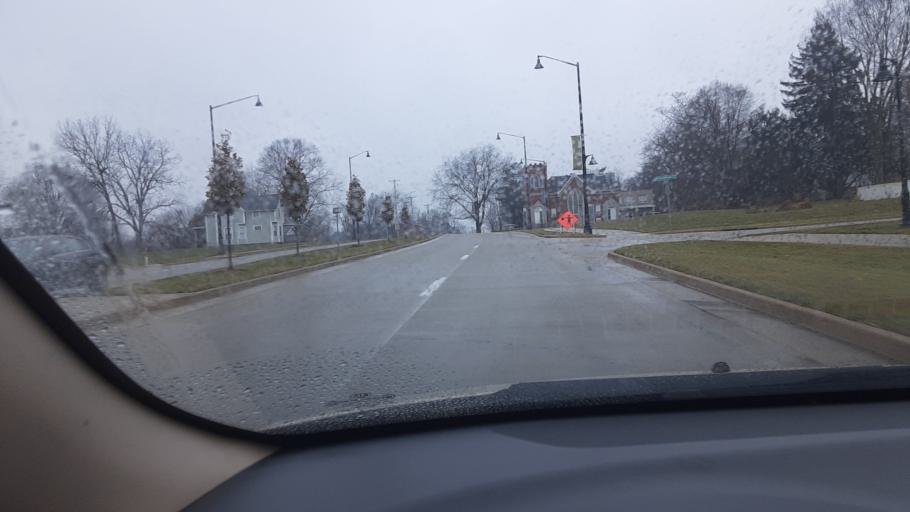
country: US
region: Illinois
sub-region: Winnebago County
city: Rockford
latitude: 42.2763
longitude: -89.1168
